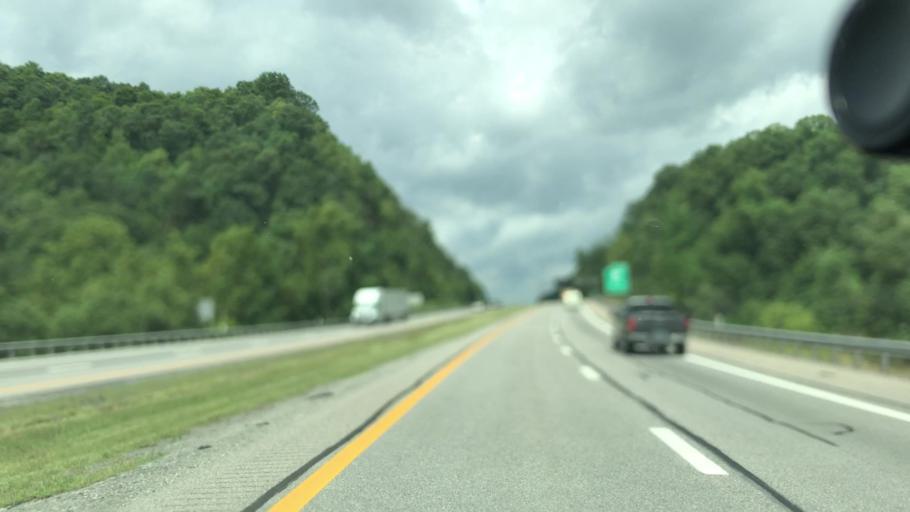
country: US
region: West Virginia
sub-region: Fayette County
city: Oak Hill
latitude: 37.9638
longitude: -81.2682
